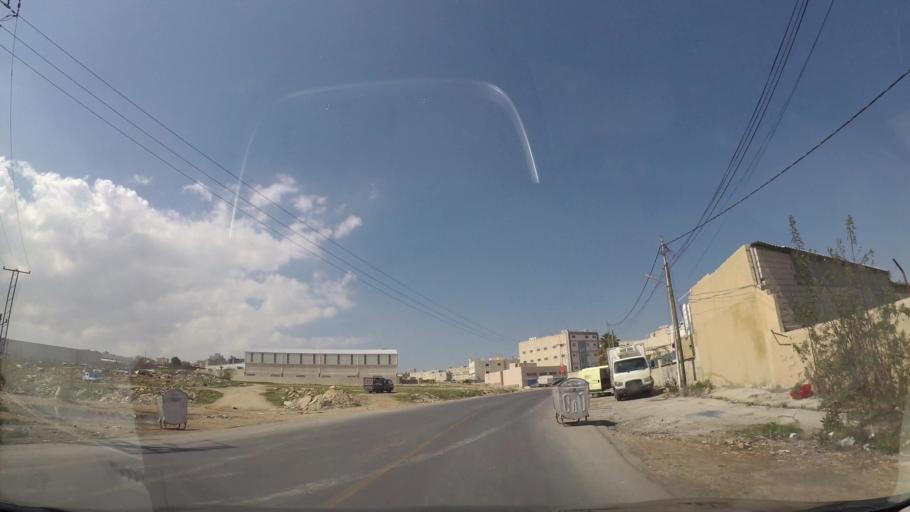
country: JO
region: Zarqa
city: Russeifa
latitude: 31.9904
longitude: 36.0139
